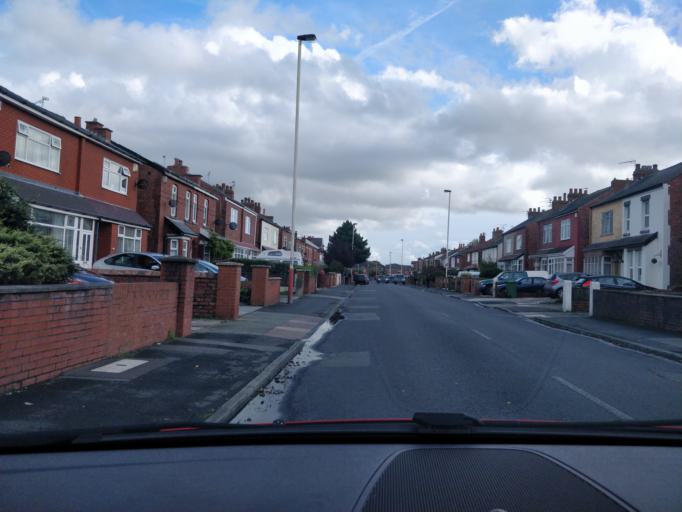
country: GB
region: England
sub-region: Sefton
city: Southport
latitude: 53.6256
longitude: -3.0043
